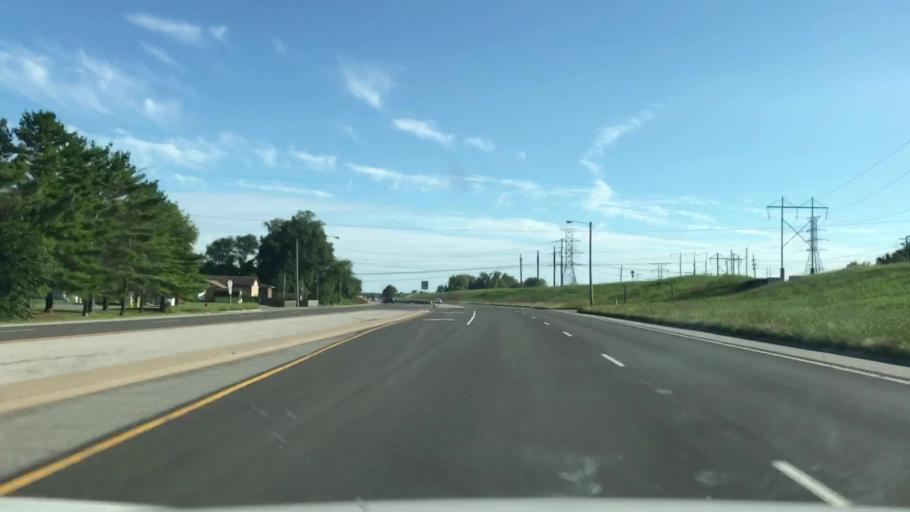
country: US
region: Illinois
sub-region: Madison County
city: Hartford
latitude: 38.8287
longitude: -90.1006
